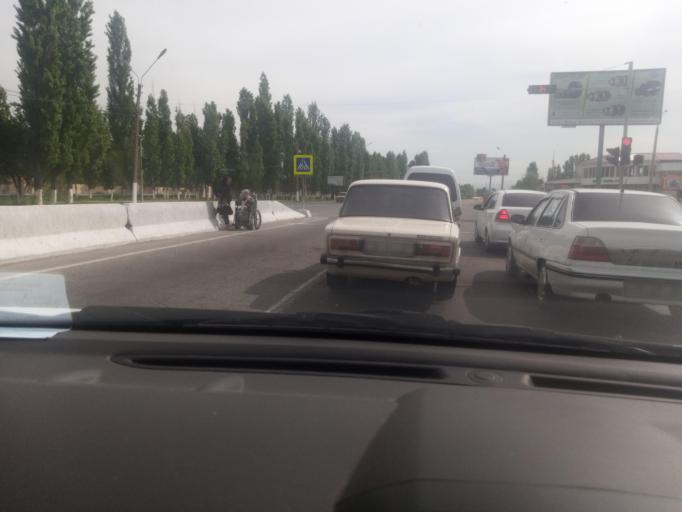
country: UZ
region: Toshkent
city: Angren
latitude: 40.9909
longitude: 70.0427
